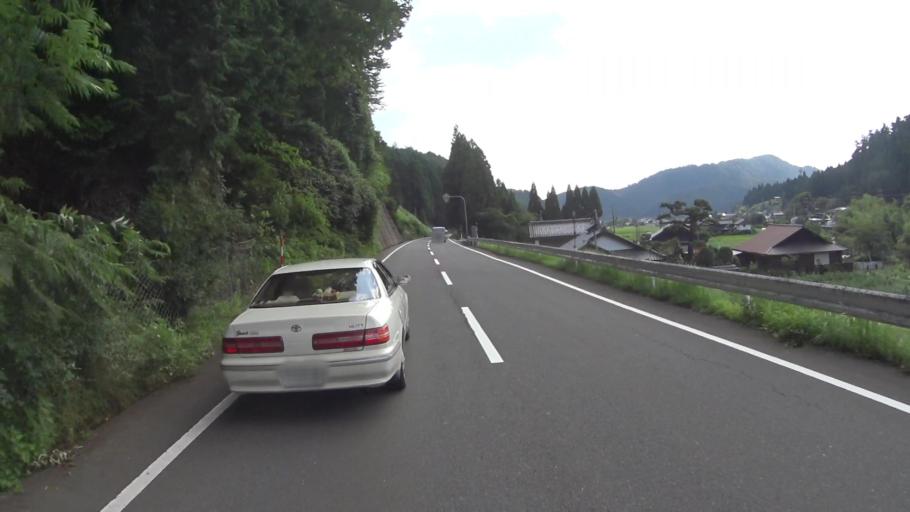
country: JP
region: Kyoto
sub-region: Kyoto-shi
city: Kamigyo-ku
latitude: 35.2213
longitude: 135.6507
